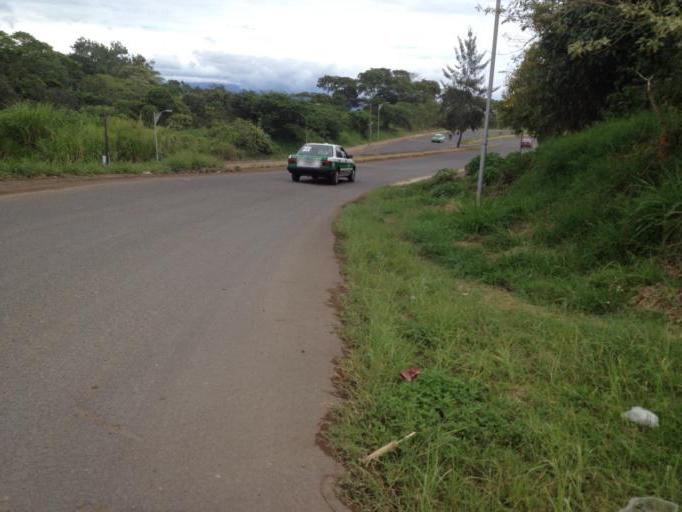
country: MX
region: Veracruz
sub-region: Emiliano Zapata
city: Las Trancas
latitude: 19.5035
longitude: -96.8609
